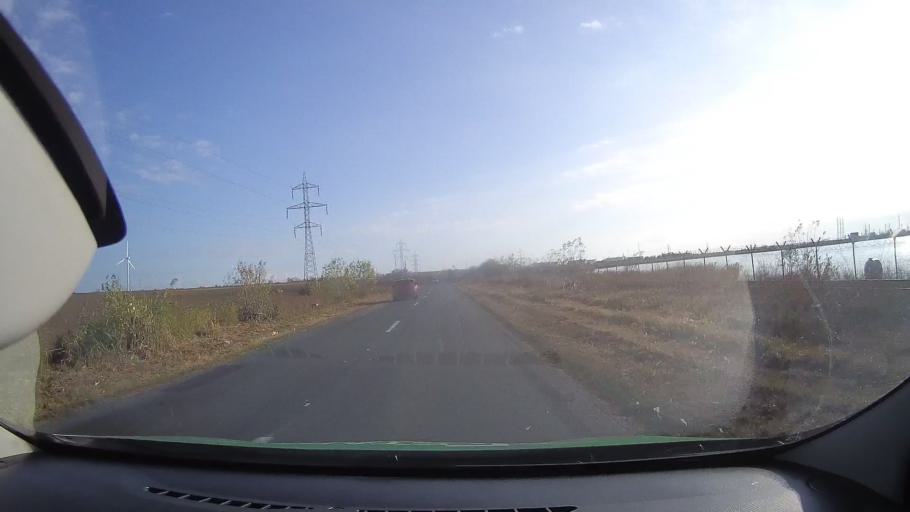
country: RO
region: Constanta
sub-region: Comuna Corbu
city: Corbu
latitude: 44.3640
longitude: 28.6734
